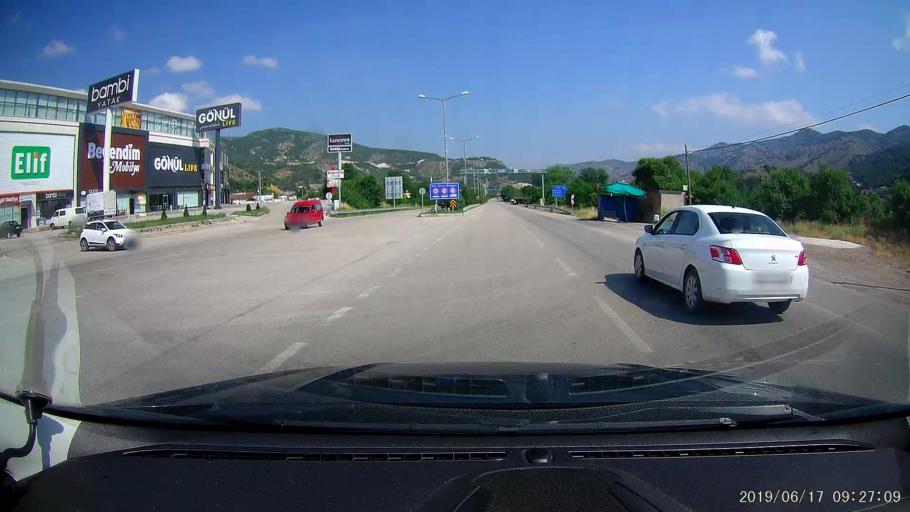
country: TR
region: Amasya
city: Amasya
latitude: 40.6743
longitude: 35.8287
